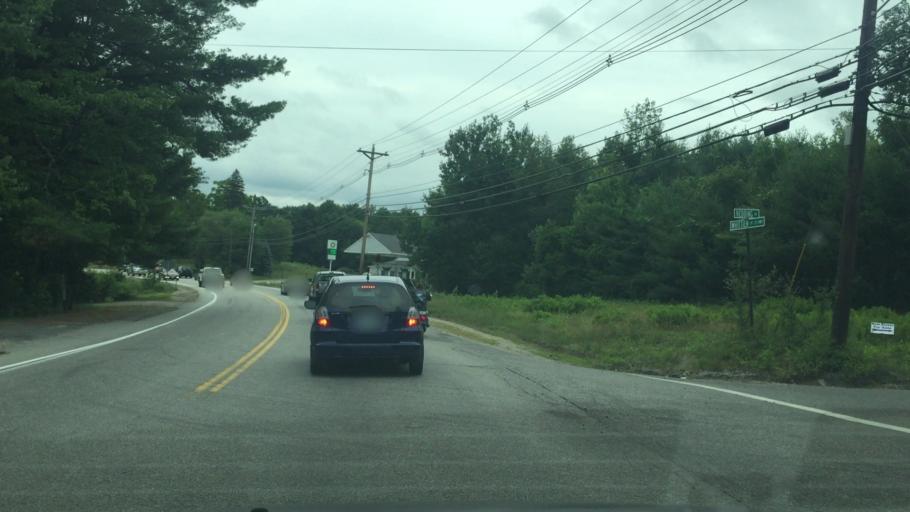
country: US
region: New Hampshire
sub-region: Carroll County
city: Center Harbor
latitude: 43.7163
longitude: -71.4388
